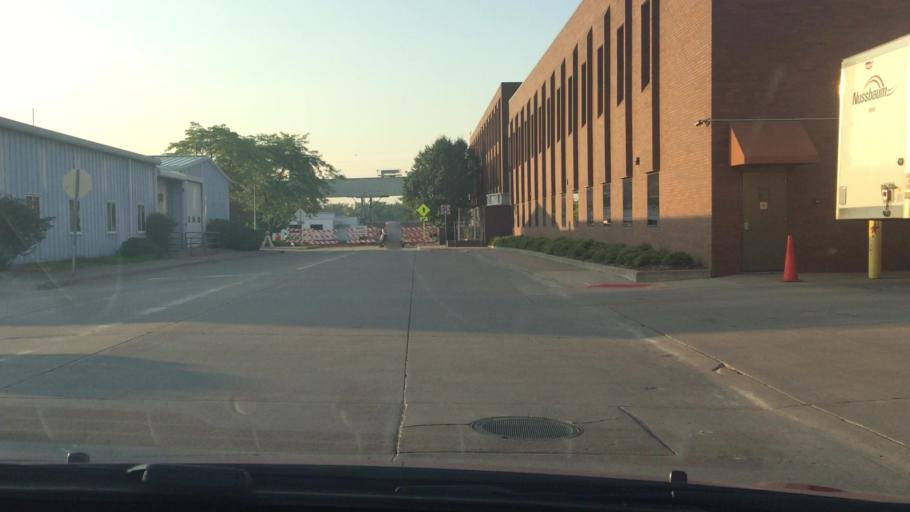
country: US
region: Iowa
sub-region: Muscatine County
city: Muscatine
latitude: 41.4257
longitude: -91.0402
